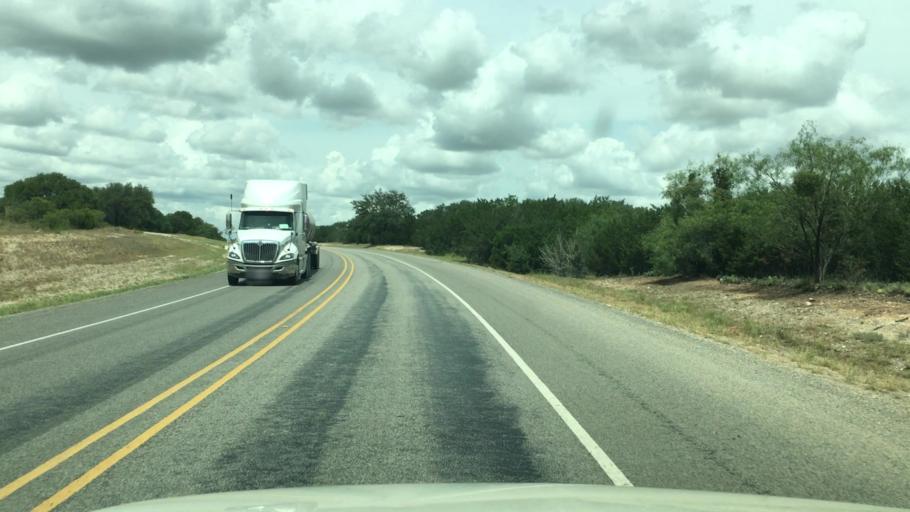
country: US
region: Texas
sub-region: McCulloch County
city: Brady
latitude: 31.0184
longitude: -99.2119
